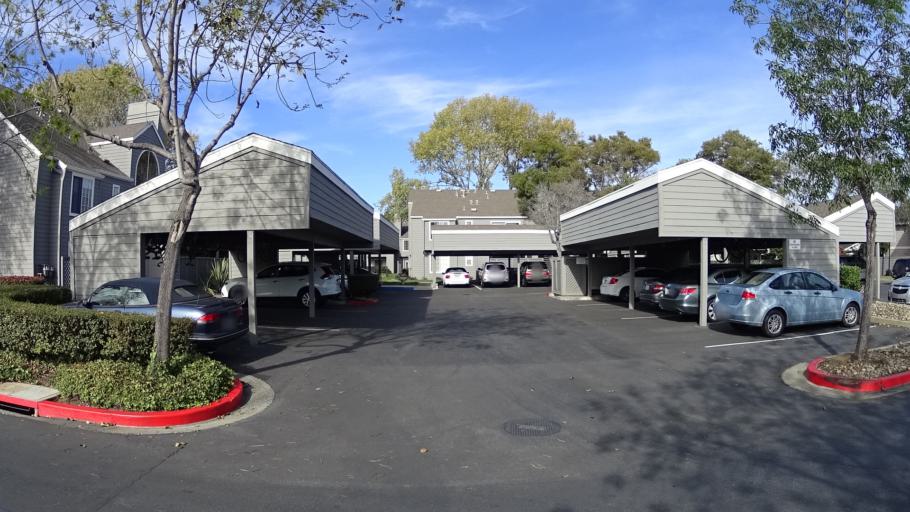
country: US
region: California
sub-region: San Mateo County
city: Belmont
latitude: 37.5345
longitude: -122.2707
